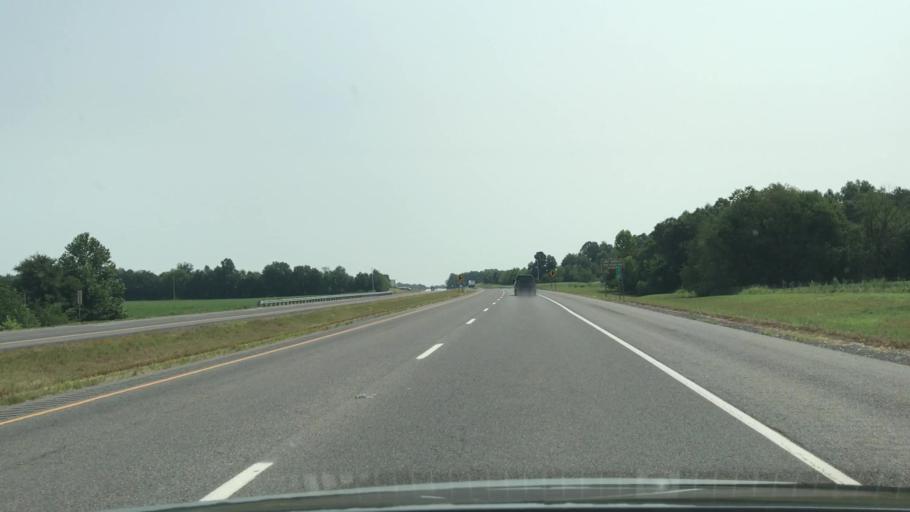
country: US
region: Kentucky
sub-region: Calloway County
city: Murray
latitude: 36.6491
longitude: -88.2416
